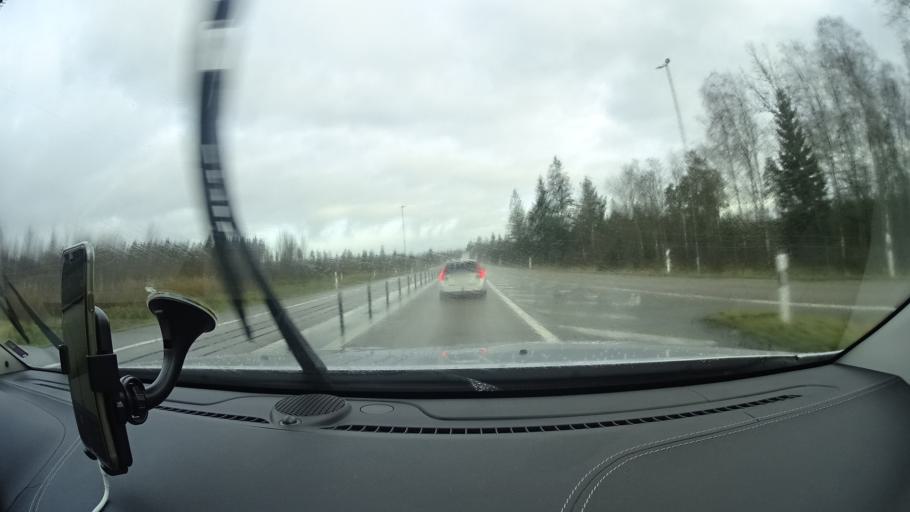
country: SE
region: Kronoberg
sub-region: Ljungby Kommun
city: Ljungby
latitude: 56.8593
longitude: 13.9451
